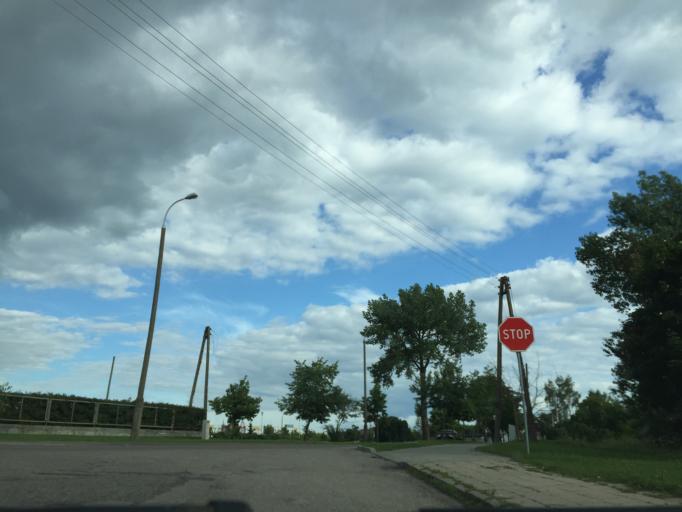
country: PL
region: Podlasie
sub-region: Suwalki
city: Suwalki
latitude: 54.1178
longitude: 22.9243
